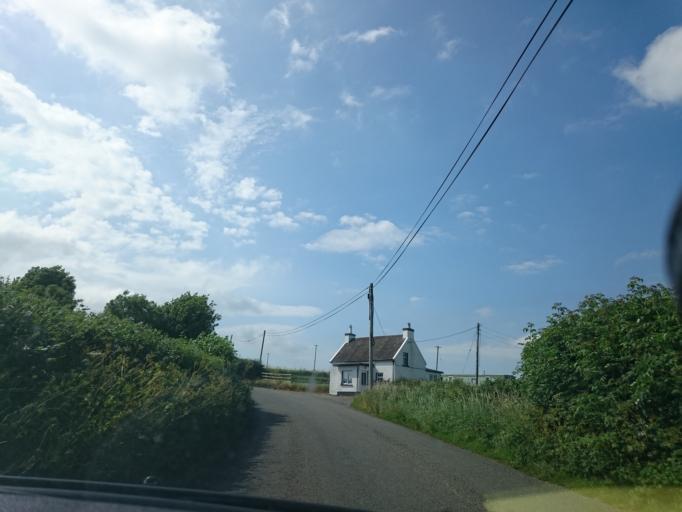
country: IE
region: Leinster
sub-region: Kilkenny
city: Thomastown
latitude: 52.5238
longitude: -7.2001
